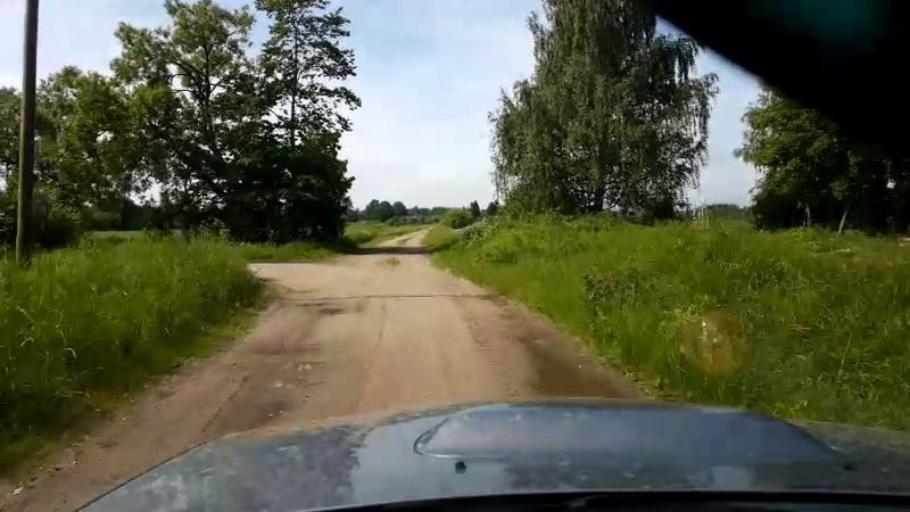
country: EE
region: Paernumaa
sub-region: Tootsi vald
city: Tootsi
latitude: 58.5215
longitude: 24.7004
